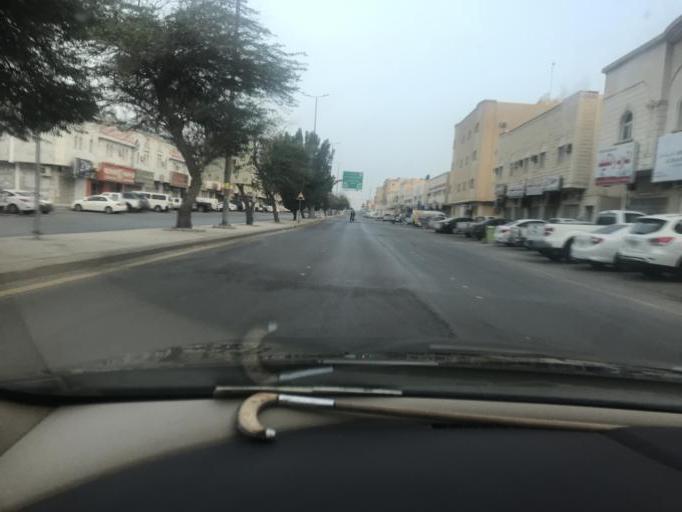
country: SA
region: Ar Riyad
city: Riyadh
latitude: 24.7301
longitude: 46.7629
